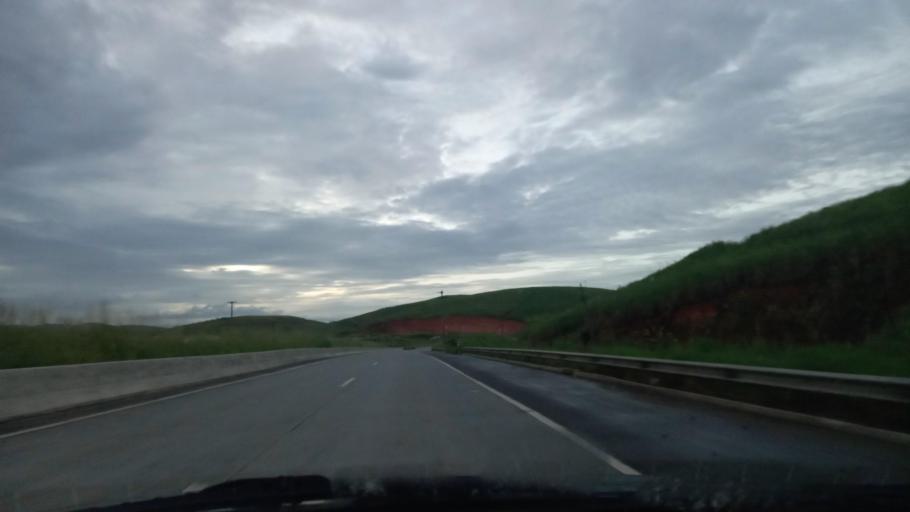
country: BR
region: Pernambuco
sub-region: Ribeirao
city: Ribeirao
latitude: -8.5209
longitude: -35.3889
